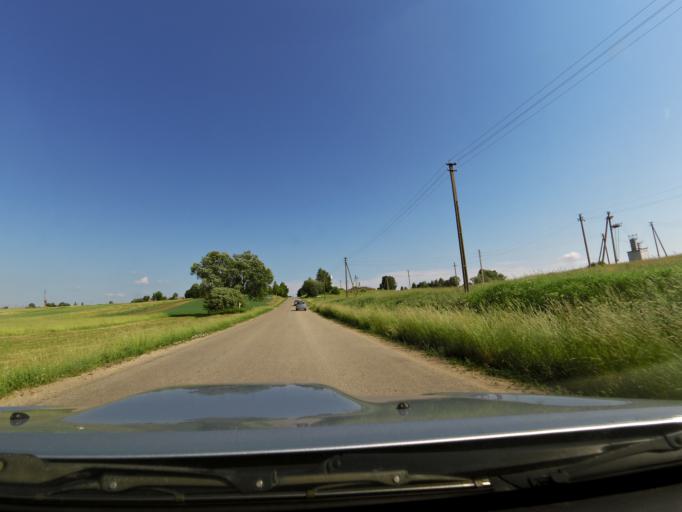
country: LT
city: Vilkaviskis
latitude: 54.5027
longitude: 23.0165
